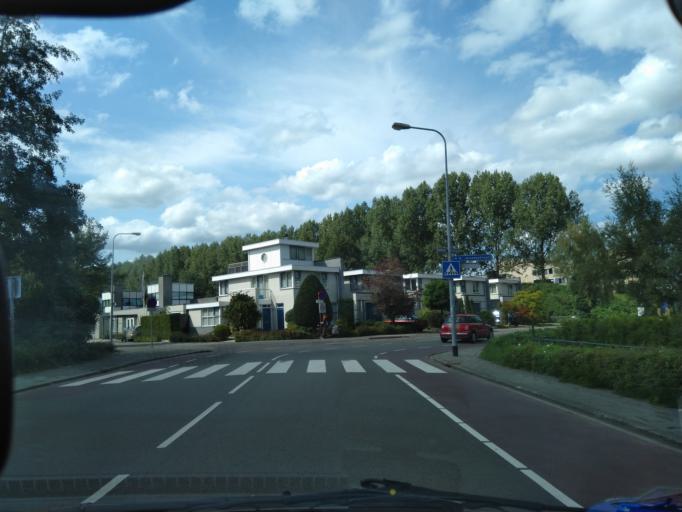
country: NL
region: Groningen
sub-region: Gemeente Groningen
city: Groningen
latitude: 53.1881
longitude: 6.5515
